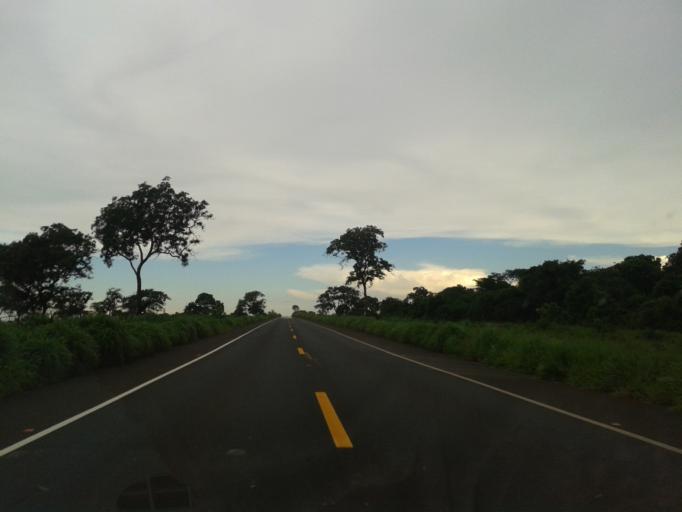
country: BR
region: Minas Gerais
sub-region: Santa Vitoria
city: Santa Vitoria
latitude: -18.9155
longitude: -50.2331
